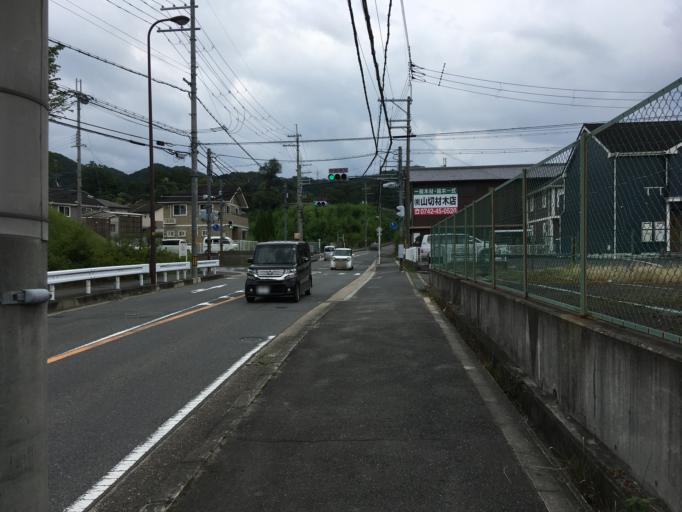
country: JP
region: Nara
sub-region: Ikoma-shi
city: Ikoma
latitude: 34.6651
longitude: 135.7171
